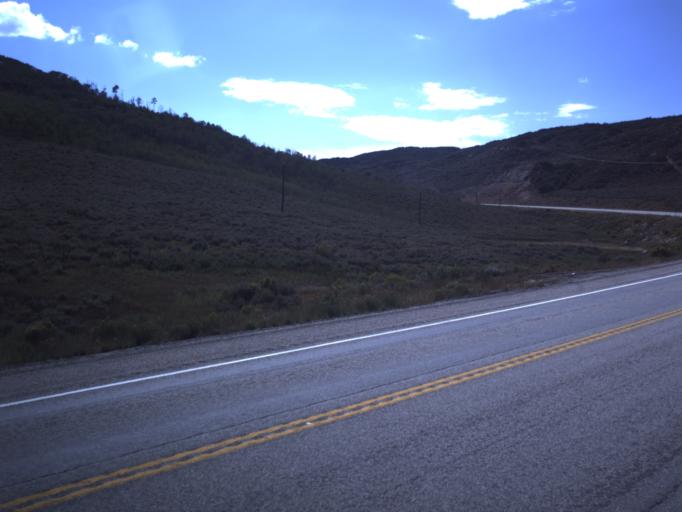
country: US
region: Utah
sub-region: Summit County
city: Francis
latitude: 40.2042
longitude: -110.9719
